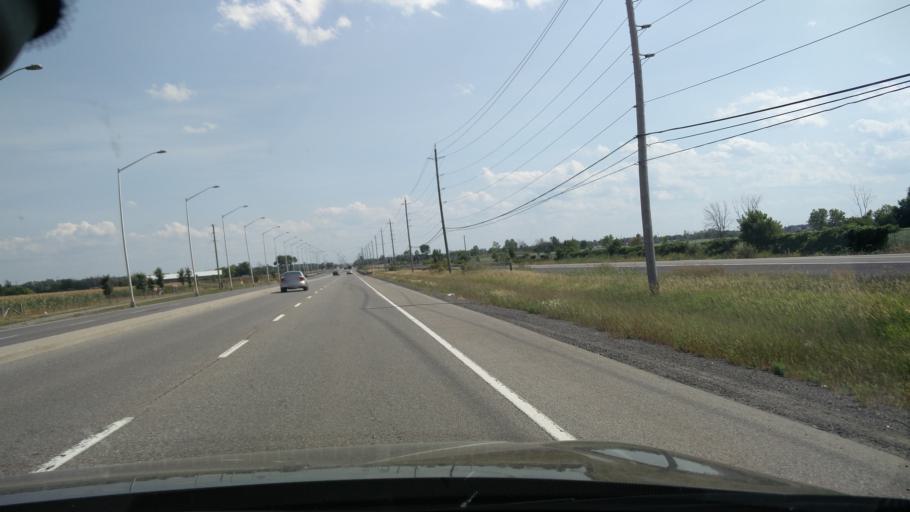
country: CA
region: Ontario
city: Bells Corners
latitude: 45.3087
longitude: -75.7371
